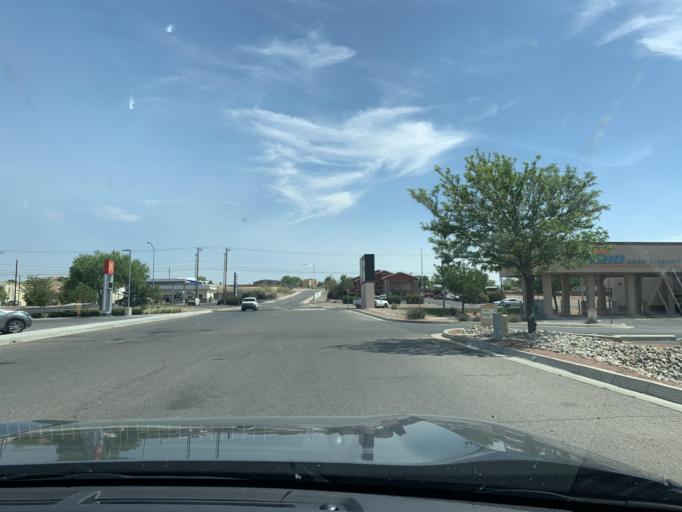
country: US
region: New Mexico
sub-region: Valencia County
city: Los Lunas
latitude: 34.8147
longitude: -106.7550
